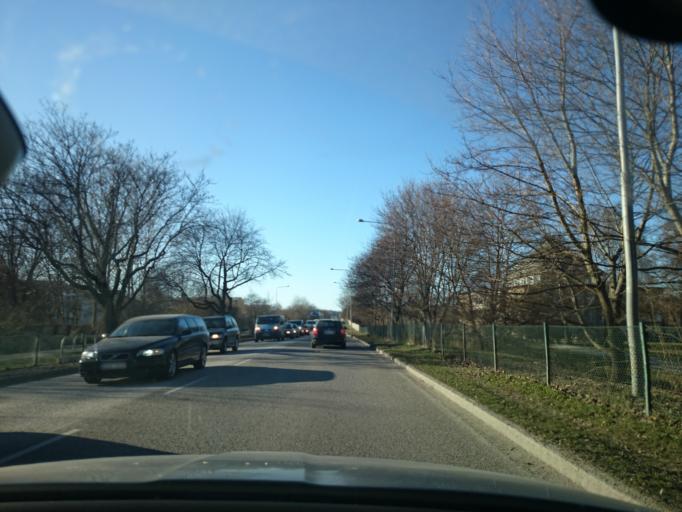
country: SE
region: Stockholm
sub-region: Huddinge Kommun
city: Huddinge
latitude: 59.2827
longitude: 17.9967
